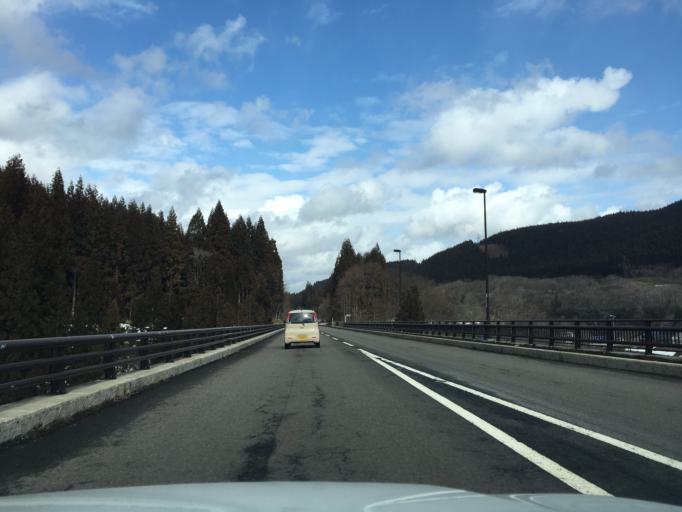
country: JP
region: Akita
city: Takanosu
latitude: 40.0091
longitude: 140.2787
